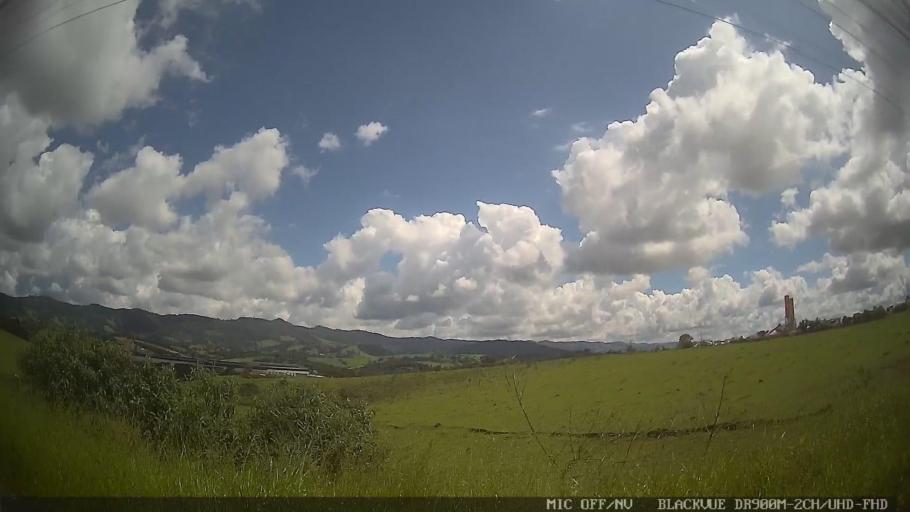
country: BR
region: Minas Gerais
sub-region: Extrema
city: Extrema
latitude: -22.8732
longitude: -46.3496
